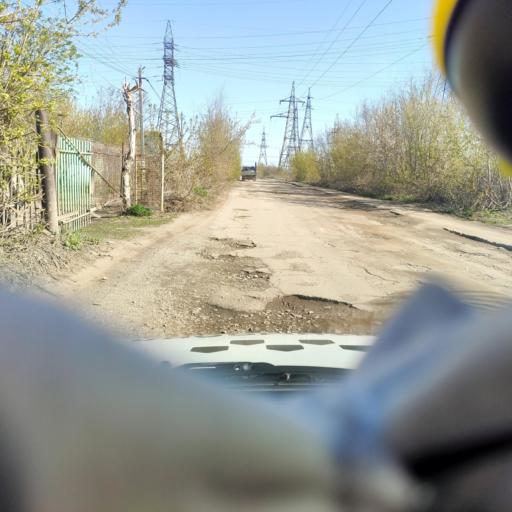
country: RU
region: Samara
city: Tol'yatti
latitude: 53.5866
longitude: 49.2951
